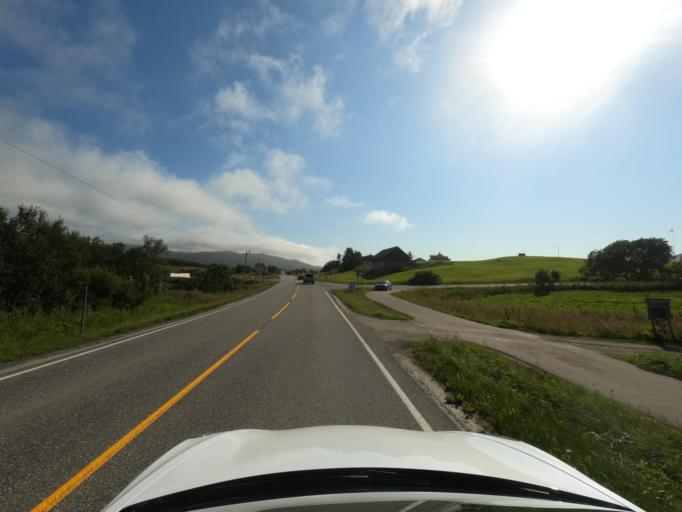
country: NO
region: Nordland
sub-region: Vestvagoy
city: Evjen
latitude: 68.2281
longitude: 13.7354
